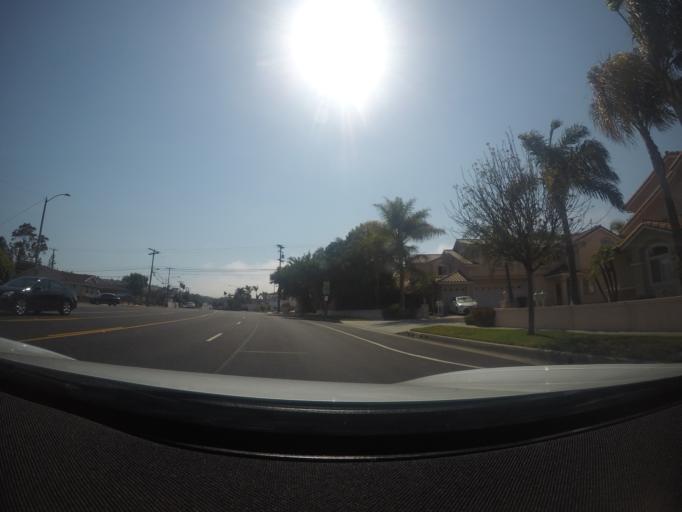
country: US
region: California
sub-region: Los Angeles County
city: Torrance
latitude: 33.8171
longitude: -118.3614
